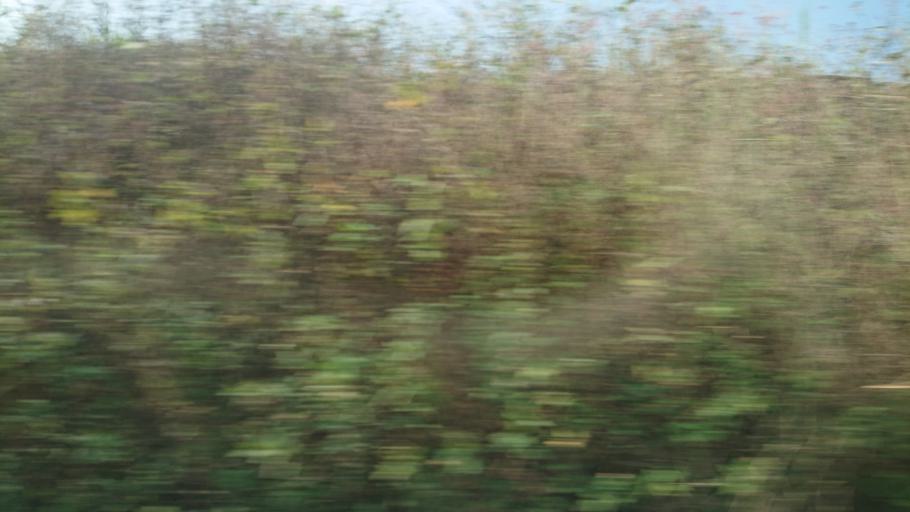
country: TW
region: Taiwan
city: Lugu
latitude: 23.7331
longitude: 120.6599
